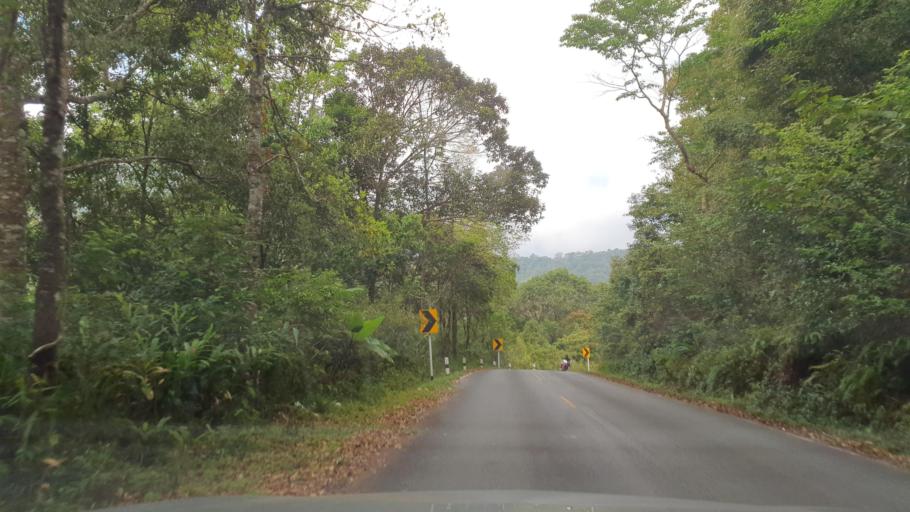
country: TH
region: Lampang
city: Mueang Pan
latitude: 18.9357
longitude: 99.3883
